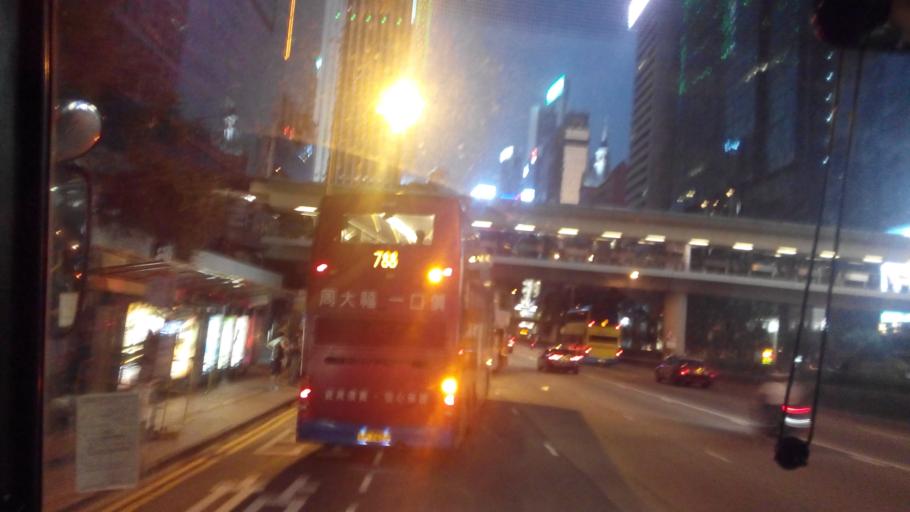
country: HK
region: Wanchai
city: Wan Chai
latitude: 22.2795
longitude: 114.1727
